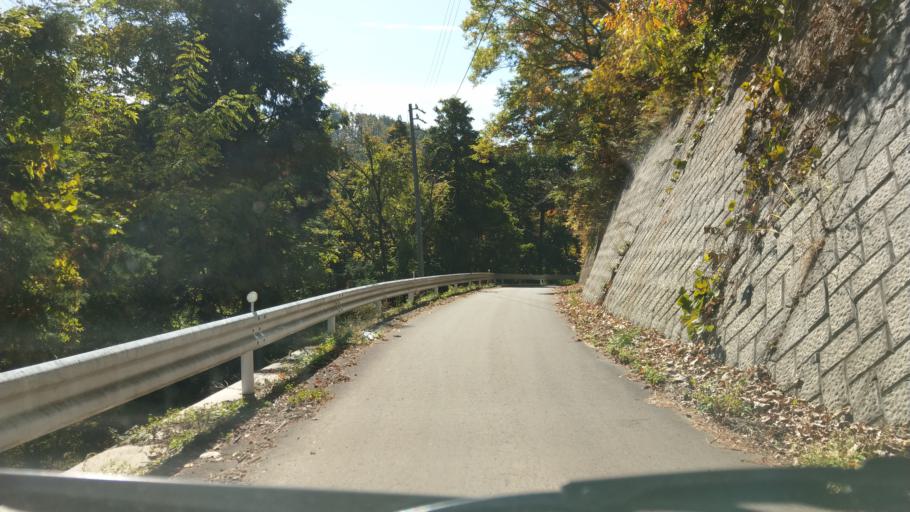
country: JP
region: Nagano
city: Komoro
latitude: 36.3759
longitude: 138.4183
